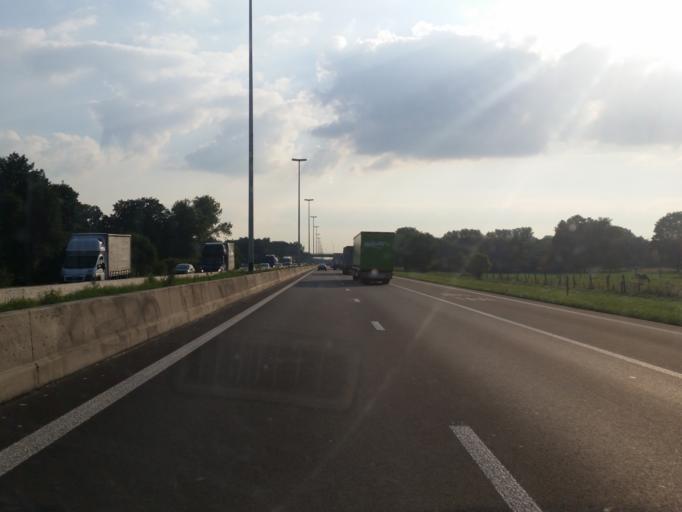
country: BE
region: Flanders
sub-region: Provincie Antwerpen
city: Zandhoven
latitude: 51.2344
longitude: 4.6653
